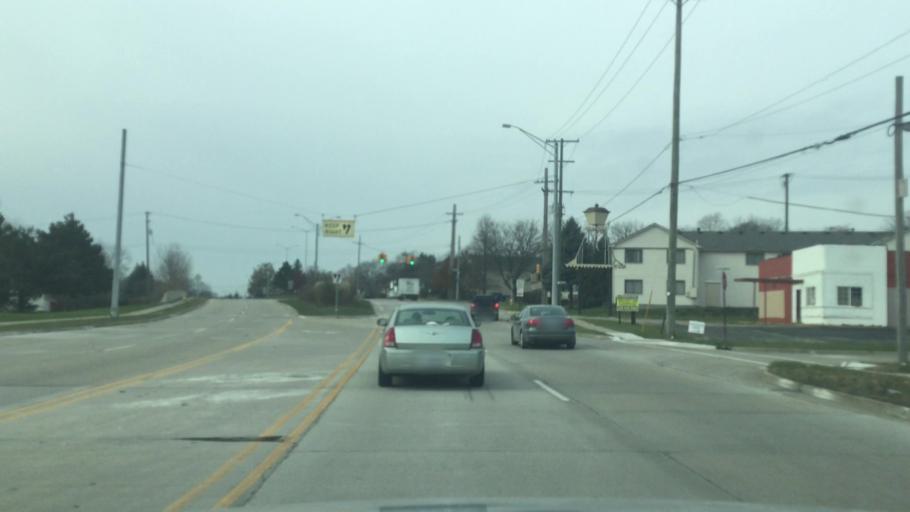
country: US
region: Michigan
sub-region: Oakland County
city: Pontiac
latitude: 42.6343
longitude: -83.2974
